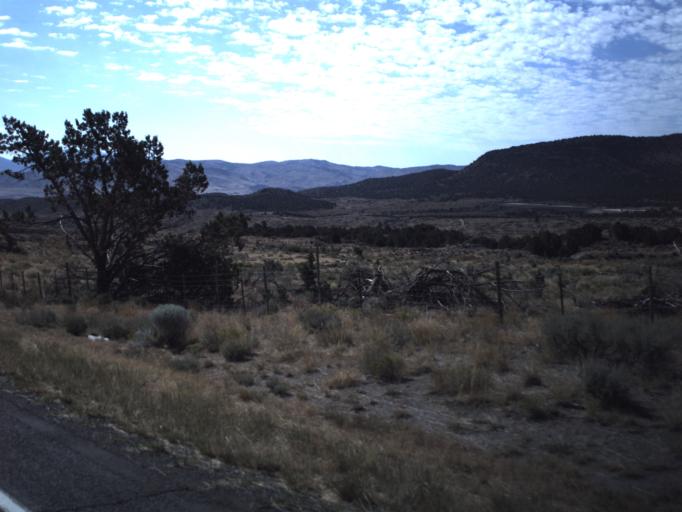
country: US
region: Utah
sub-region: Utah County
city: Genola
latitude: 39.9640
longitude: -112.0451
